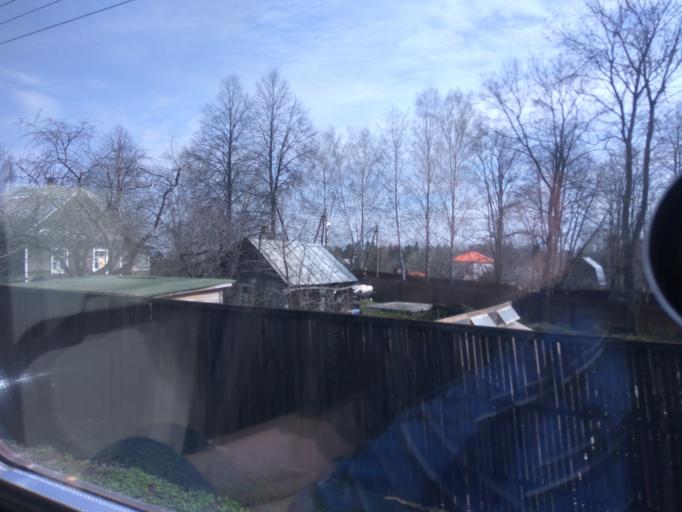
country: RU
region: Moskovskaya
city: Yermolino
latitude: 56.1307
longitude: 37.5204
